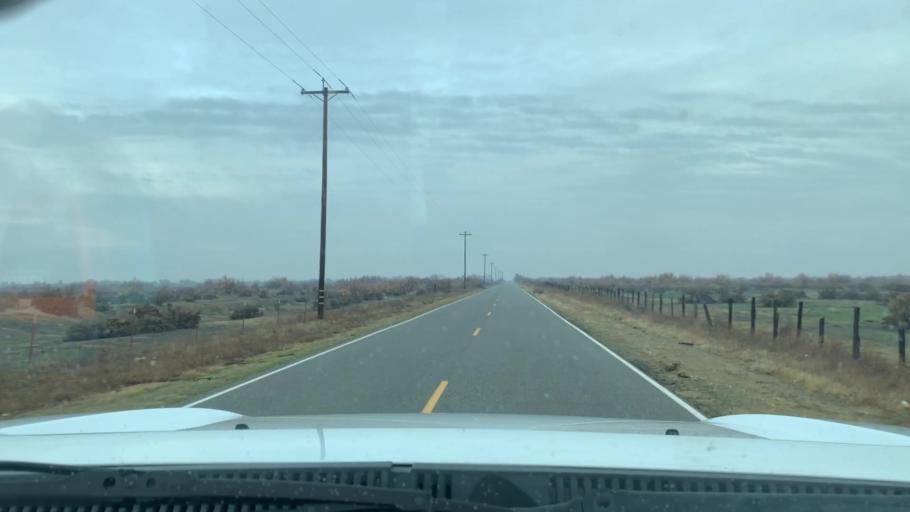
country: US
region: California
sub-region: Kern County
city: Lost Hills
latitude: 35.7083
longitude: -119.5796
